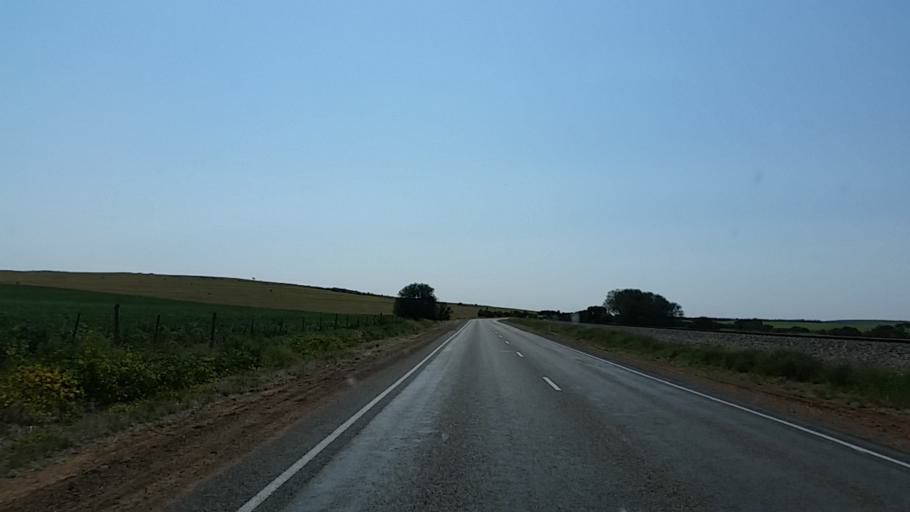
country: AU
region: South Australia
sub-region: Port Pirie City and Dists
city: Crystal Brook
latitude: -33.2445
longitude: 138.3733
